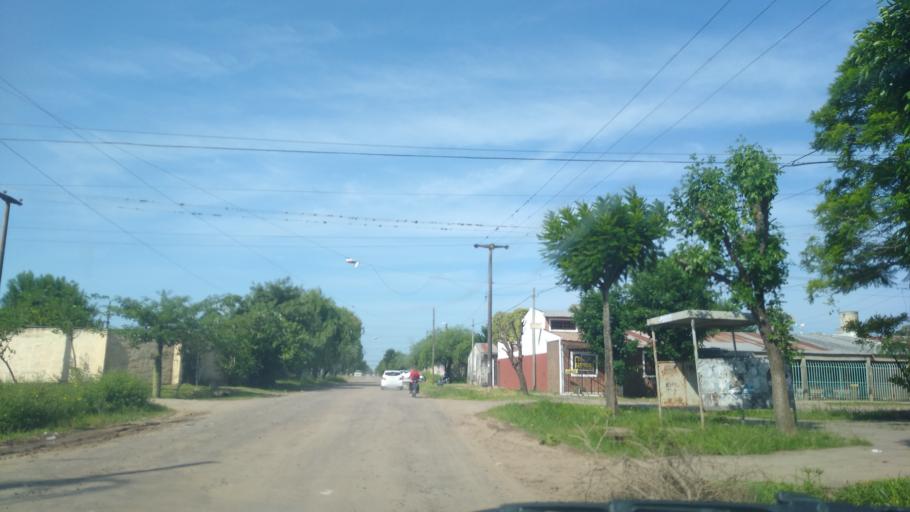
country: AR
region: Chaco
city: Barranqueras
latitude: -27.4944
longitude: -58.9542
